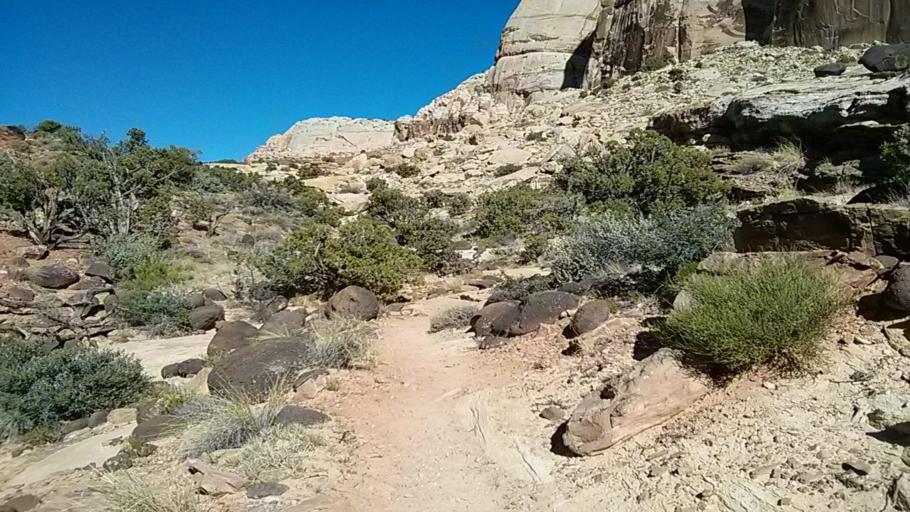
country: US
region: Utah
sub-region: Wayne County
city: Loa
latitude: 38.2918
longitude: -111.2289
